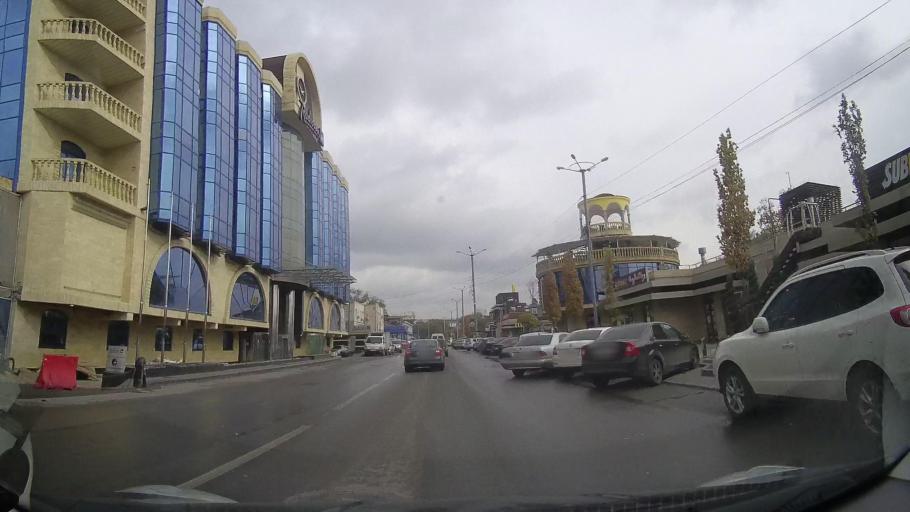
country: RU
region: Rostov
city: Rostov-na-Donu
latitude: 47.2139
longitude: 39.7143
